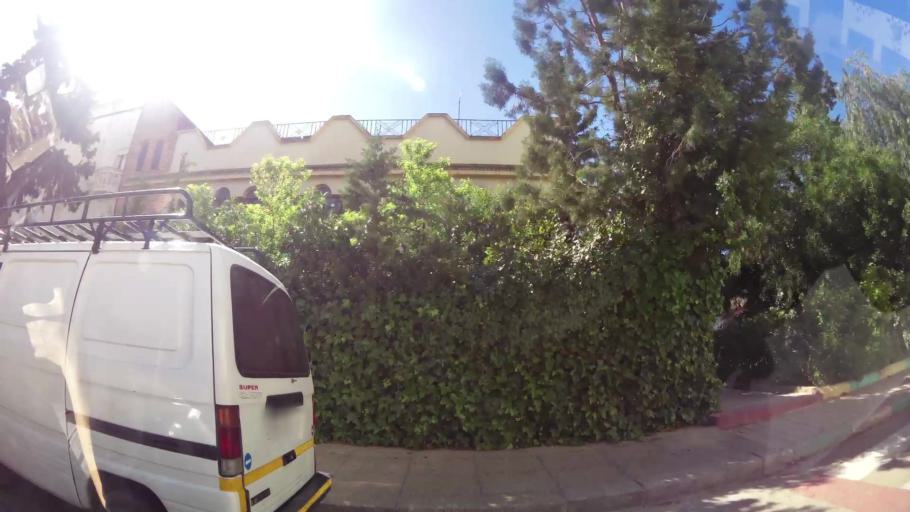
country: MA
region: Oriental
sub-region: Oujda-Angad
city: Oujda
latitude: 34.6585
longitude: -1.8964
